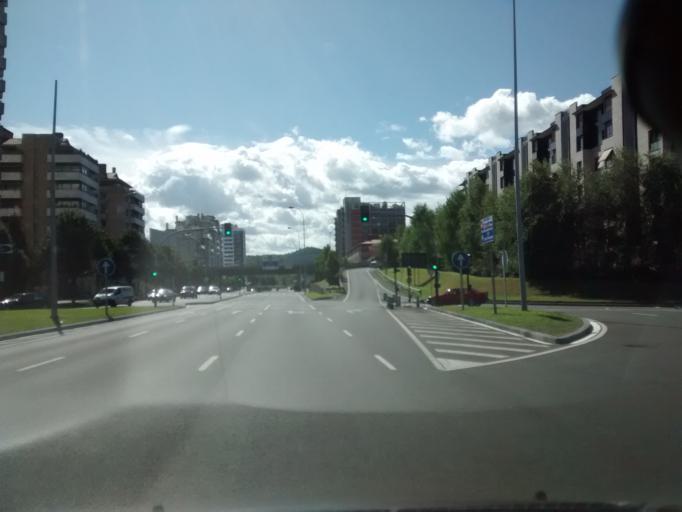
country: ES
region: Basque Country
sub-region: Provincia de Guipuzcoa
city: San Sebastian
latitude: 43.3046
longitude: -2.0062
